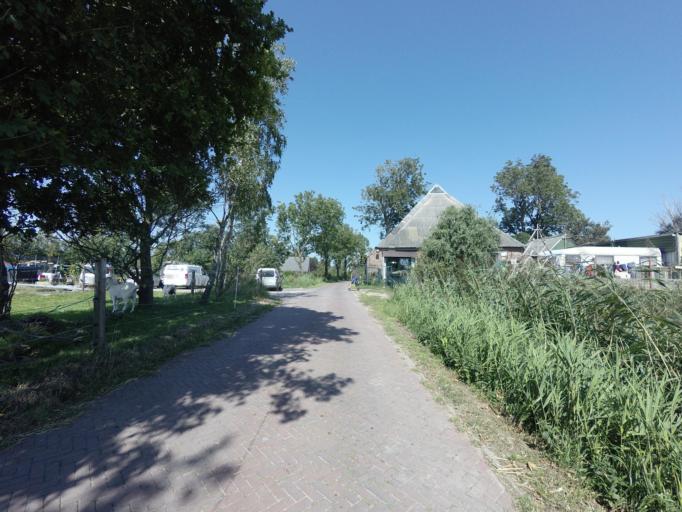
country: NL
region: Friesland
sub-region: Gemeente Dongeradeel
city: Ternaard
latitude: 53.3714
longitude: 5.9950
